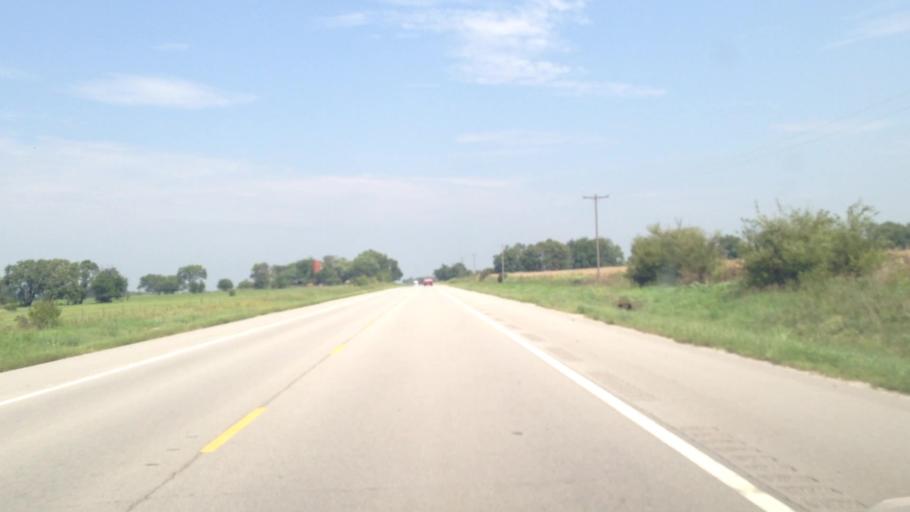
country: US
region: Kansas
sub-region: Labette County
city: Altamont
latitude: 37.2385
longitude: -95.2672
